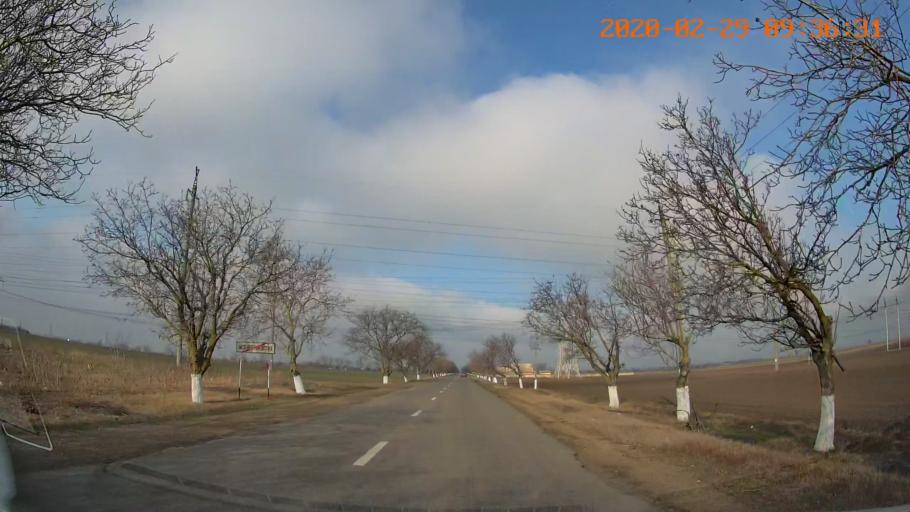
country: MD
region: Telenesti
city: Dnestrovsc
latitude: 46.6245
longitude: 29.8868
